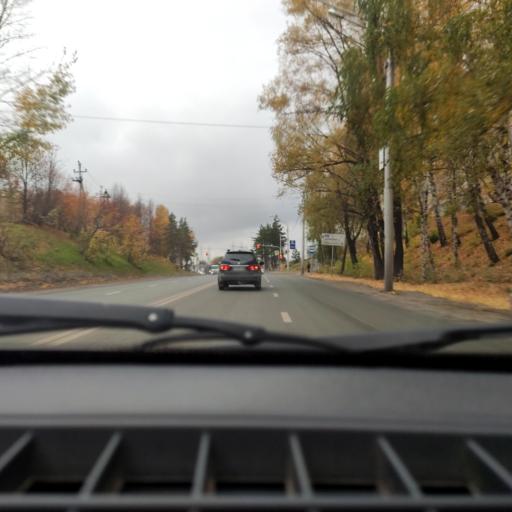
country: RU
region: Bashkortostan
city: Avdon
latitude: 54.6822
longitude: 55.8092
